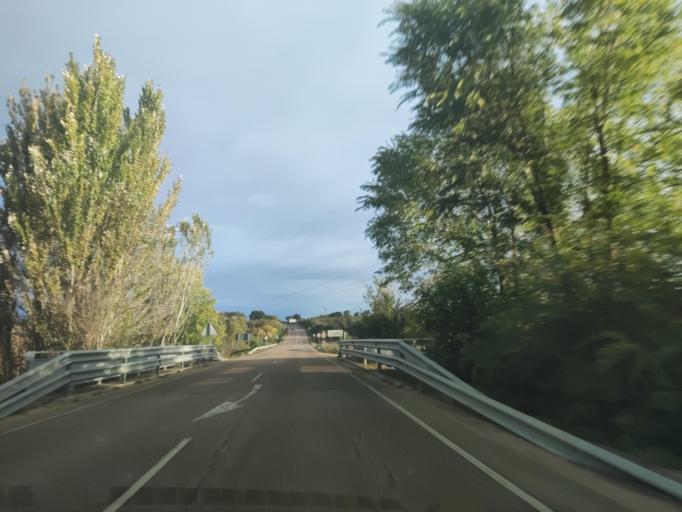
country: ES
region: Castille and Leon
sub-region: Provincia de Salamanca
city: San Felices de los Gallegos
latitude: 40.8512
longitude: -6.7037
